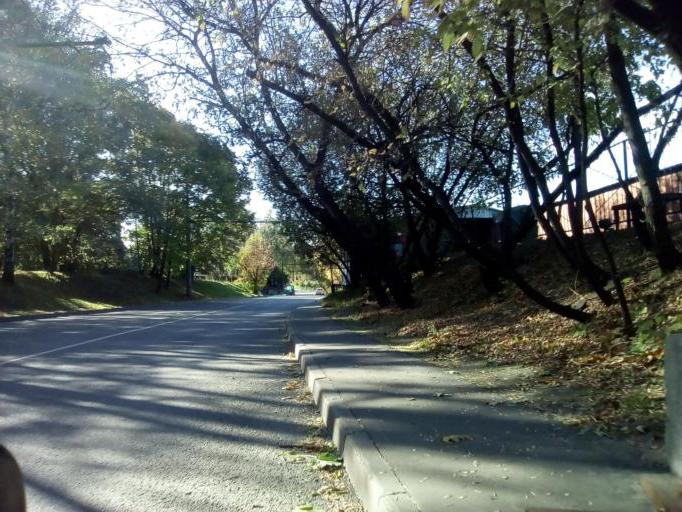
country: RU
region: Moscow
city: Novovladykino
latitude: 55.8474
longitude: 37.5839
